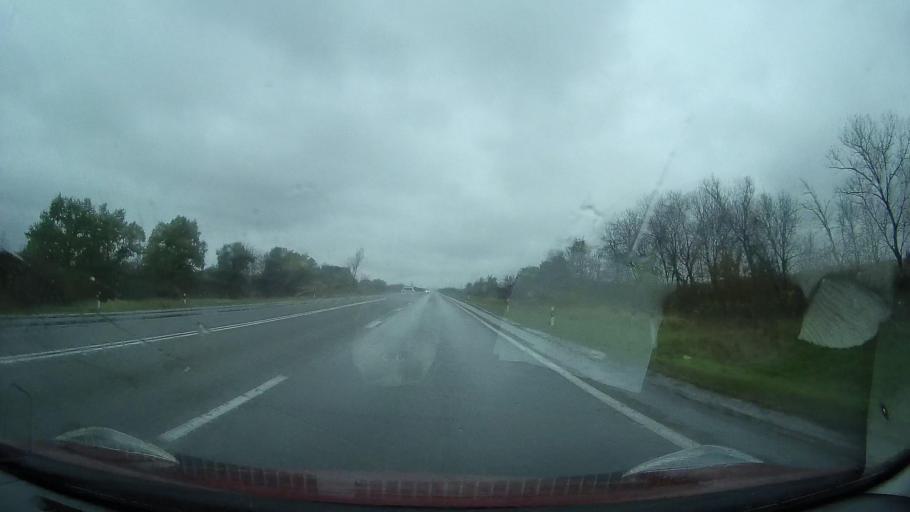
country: RU
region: Stavropol'skiy
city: Nevinnomyssk
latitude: 44.6313
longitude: 42.0243
